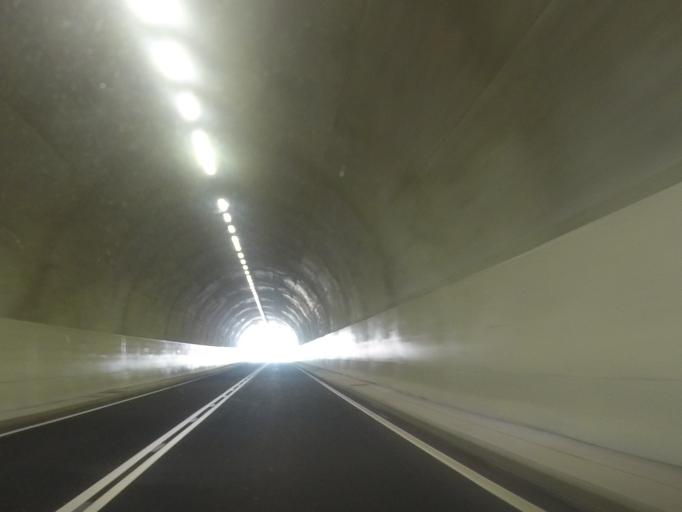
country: PT
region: Madeira
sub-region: Calheta
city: Faja da Ovelha
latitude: 32.7721
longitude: -17.2182
